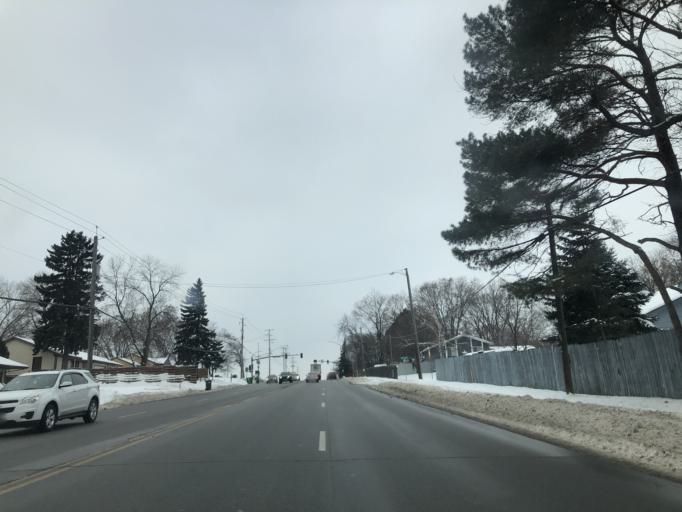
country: US
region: Minnesota
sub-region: Hennepin County
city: Osseo
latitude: 45.0946
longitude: -93.3898
